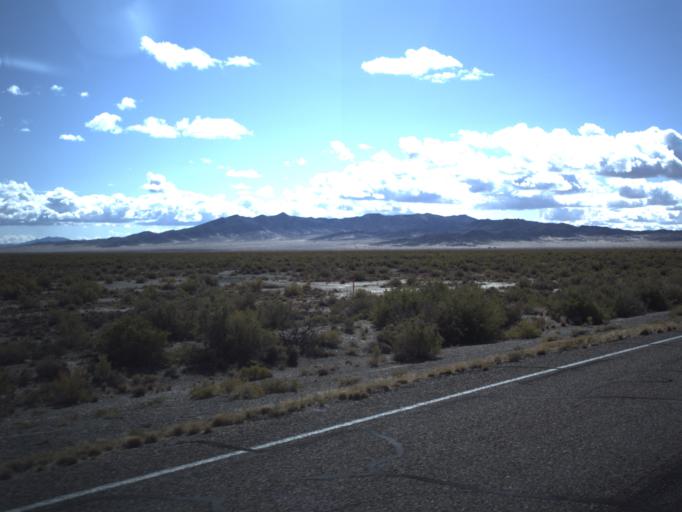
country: US
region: Nevada
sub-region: White Pine County
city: McGill
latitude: 39.0451
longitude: -114.0363
